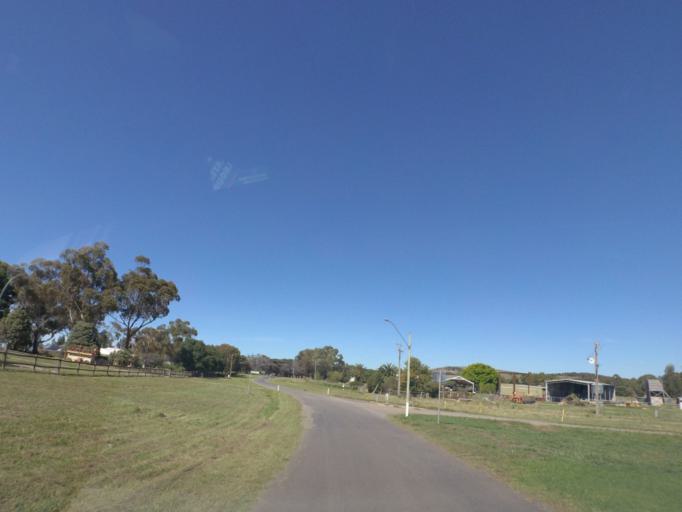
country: AU
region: Victoria
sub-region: Whittlesea
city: Whittlesea
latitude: -37.5572
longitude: 145.1232
